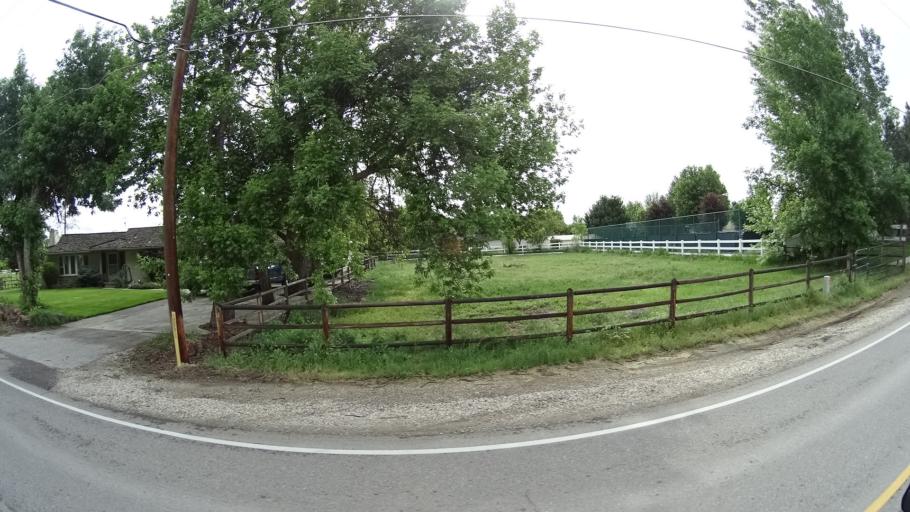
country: US
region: Idaho
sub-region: Ada County
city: Eagle
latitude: 43.7085
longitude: -116.3791
